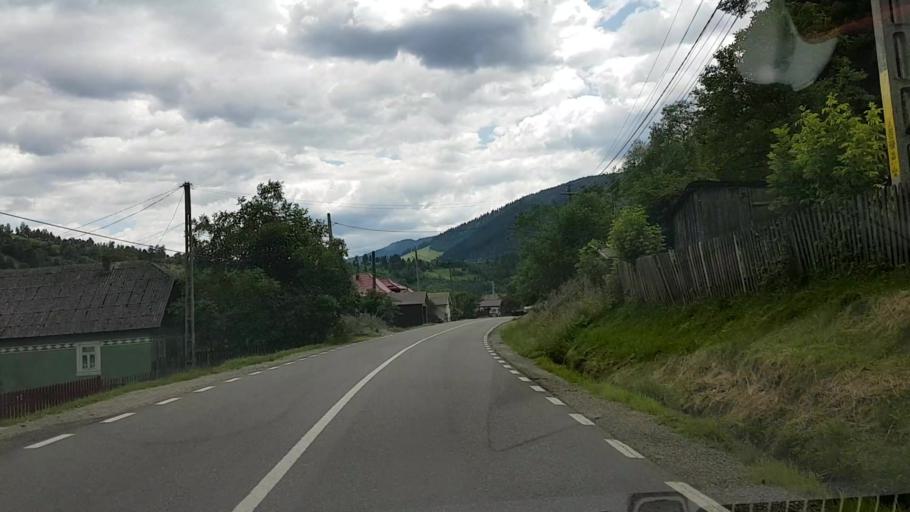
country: RO
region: Neamt
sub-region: Comuna Borca
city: Borca
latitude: 47.2142
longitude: 25.7557
